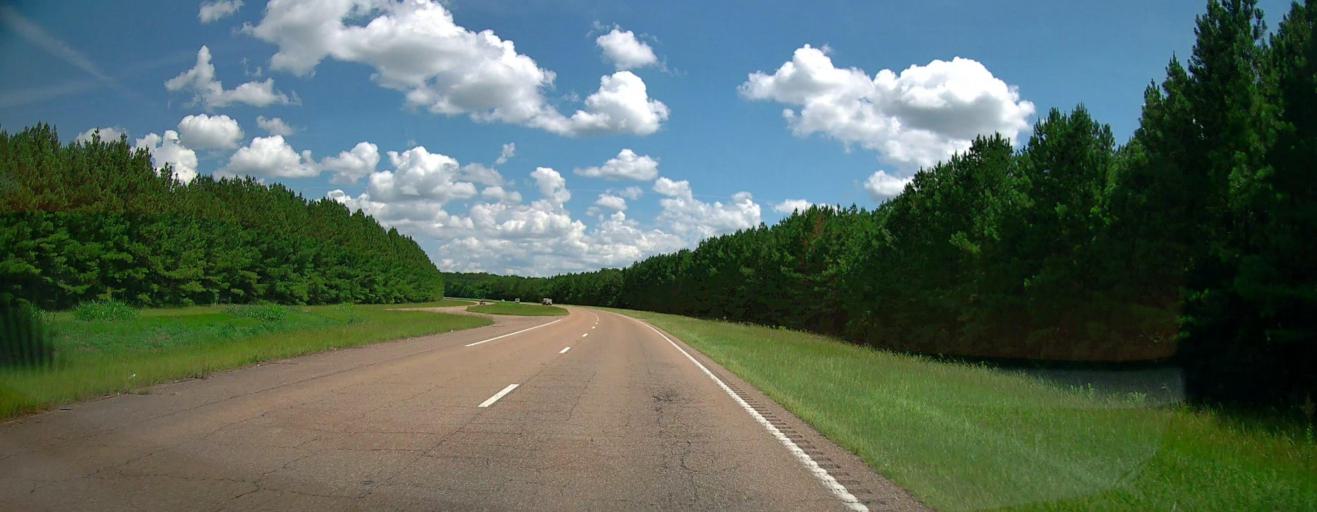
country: US
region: Mississippi
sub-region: Monroe County
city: Aberdeen
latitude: 33.8218
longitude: -88.5831
